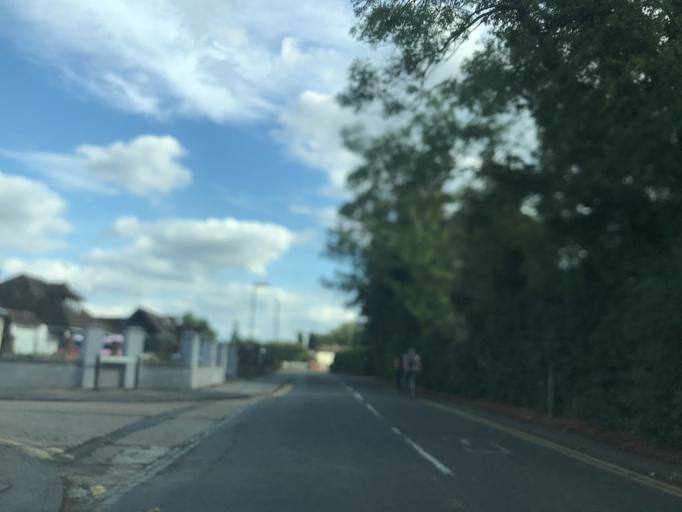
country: GB
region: England
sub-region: Surrey
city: Colnbrook
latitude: 51.4654
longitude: -0.5016
